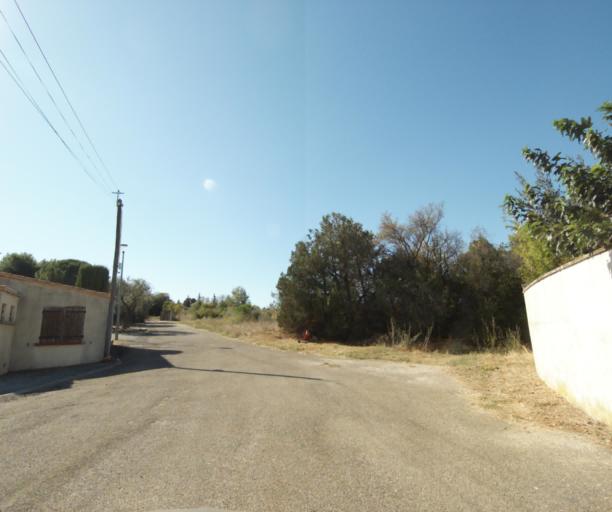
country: FR
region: Languedoc-Roussillon
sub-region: Departement du Gard
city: Bouillargues
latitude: 43.7994
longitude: 4.4170
